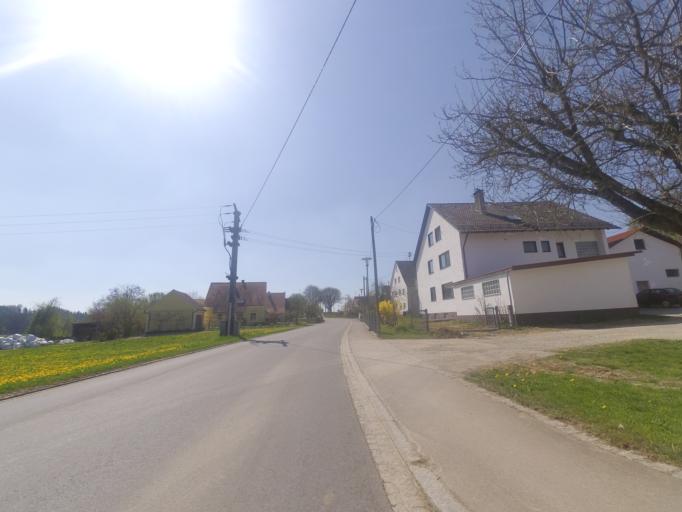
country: DE
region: Bavaria
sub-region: Swabia
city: Roggenburg
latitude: 48.2995
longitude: 10.2120
